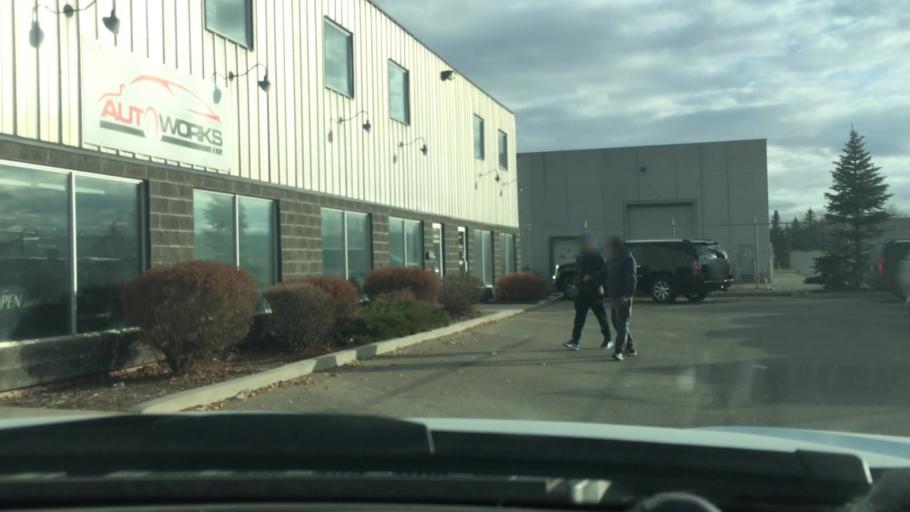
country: CA
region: Alberta
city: Calgary
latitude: 51.0022
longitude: -113.9663
